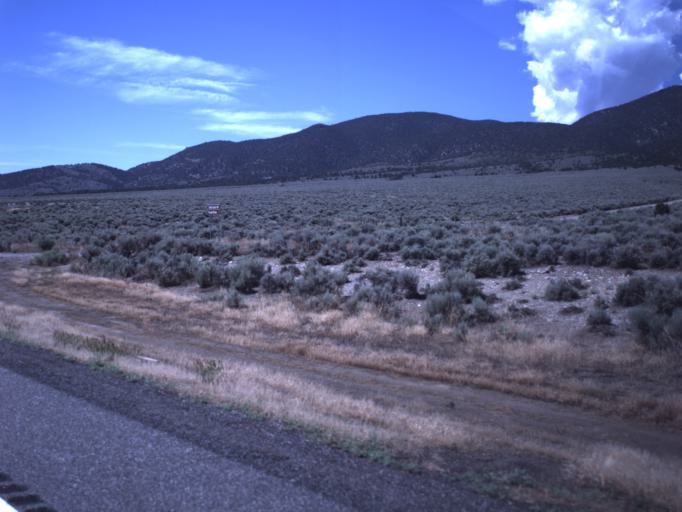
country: US
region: Utah
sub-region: Piute County
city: Junction
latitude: 38.3683
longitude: -112.2248
